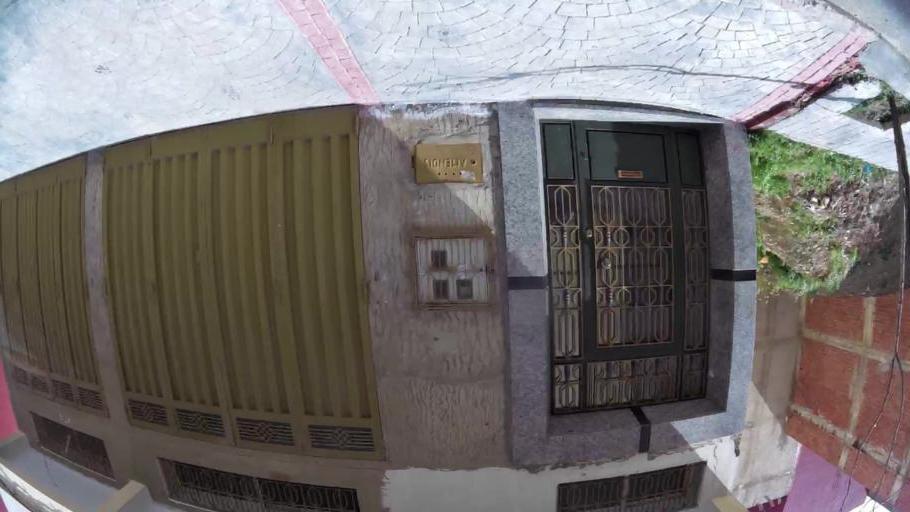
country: MA
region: Tanger-Tetouan
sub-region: Tanger-Assilah
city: Tangier
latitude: 35.7674
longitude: -5.7658
